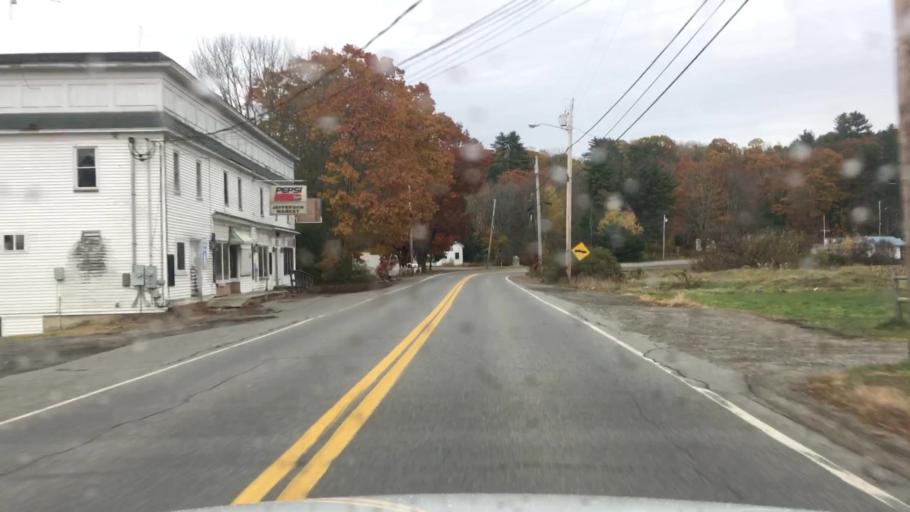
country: US
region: Maine
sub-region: Lincoln County
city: Jefferson
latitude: 44.2005
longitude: -69.4544
